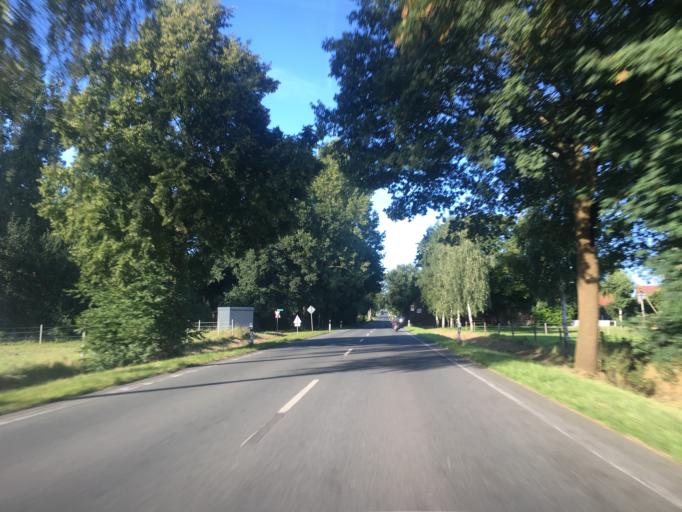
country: DE
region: North Rhine-Westphalia
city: Olfen
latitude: 51.7745
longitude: 7.3461
